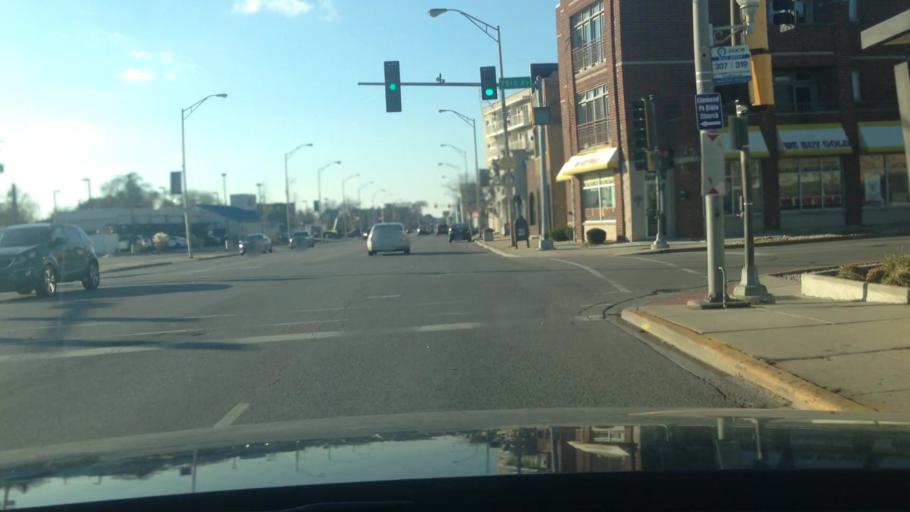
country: US
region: Illinois
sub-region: Cook County
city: Elmwood Park
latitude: 41.9252
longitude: -87.8134
